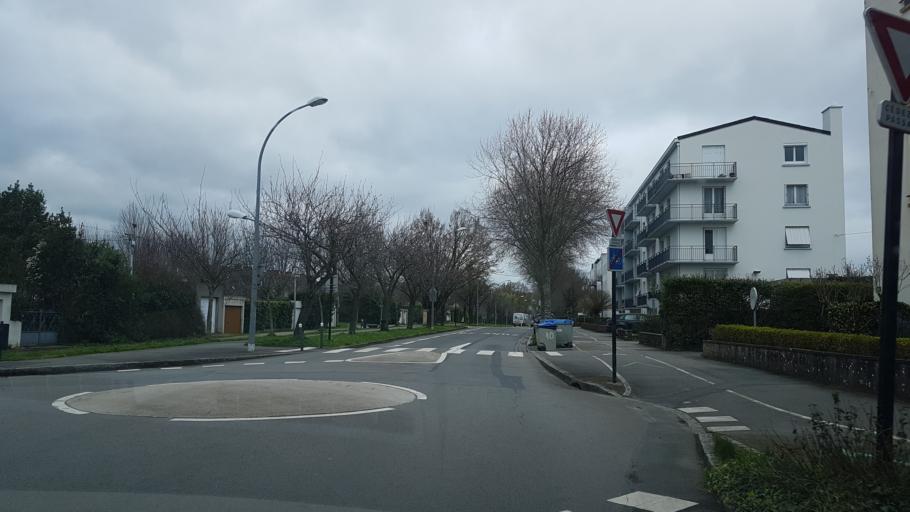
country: FR
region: Pays de la Loire
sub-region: Departement de la Loire-Atlantique
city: Nantes
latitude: 47.2436
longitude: -1.5284
